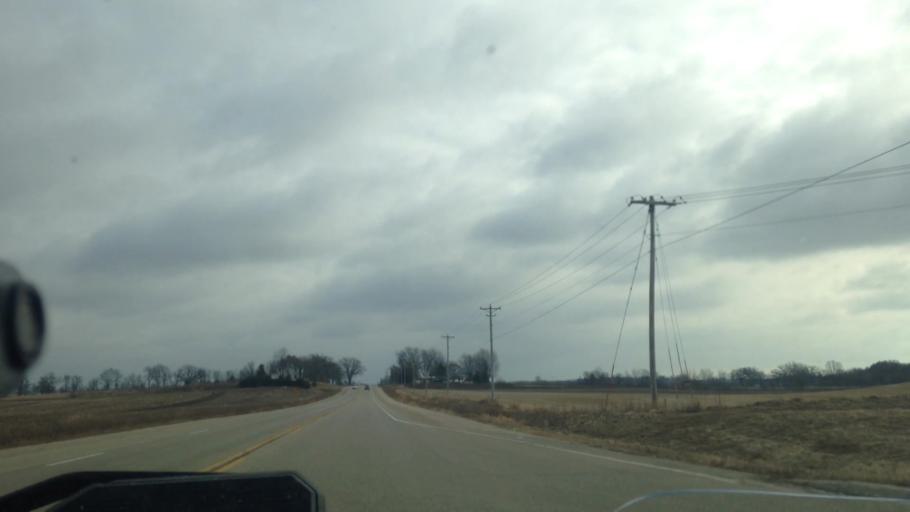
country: US
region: Wisconsin
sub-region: Dodge County
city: Horicon
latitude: 43.4439
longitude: -88.6732
